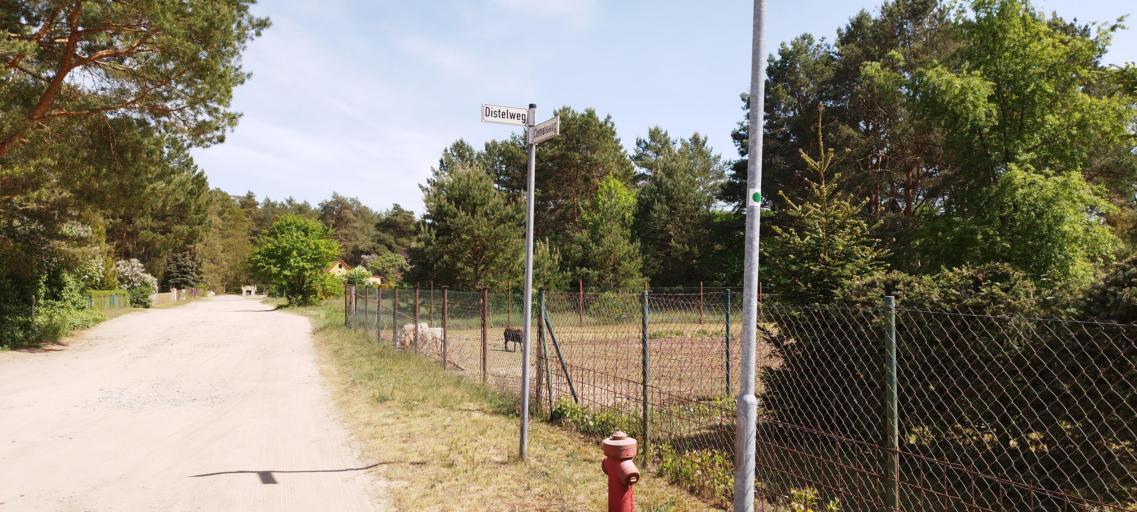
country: DE
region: Brandenburg
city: Furstenwalde
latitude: 52.3725
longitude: 14.0277
